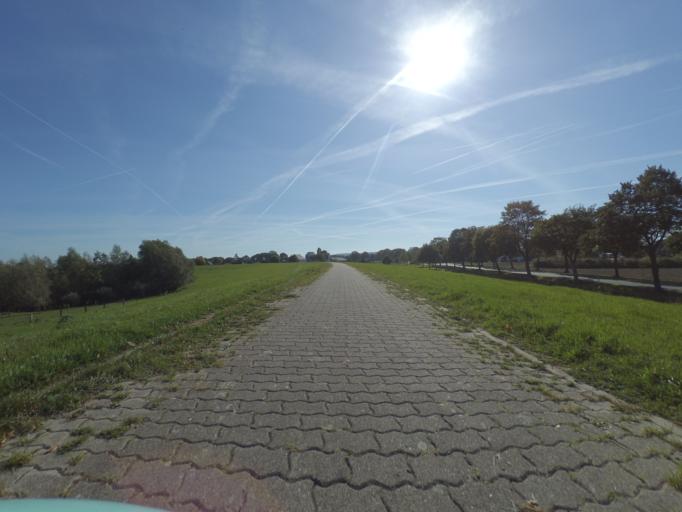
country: DE
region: North Rhine-Westphalia
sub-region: Regierungsbezirk Dusseldorf
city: Kleve
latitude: 51.8321
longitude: 6.1012
